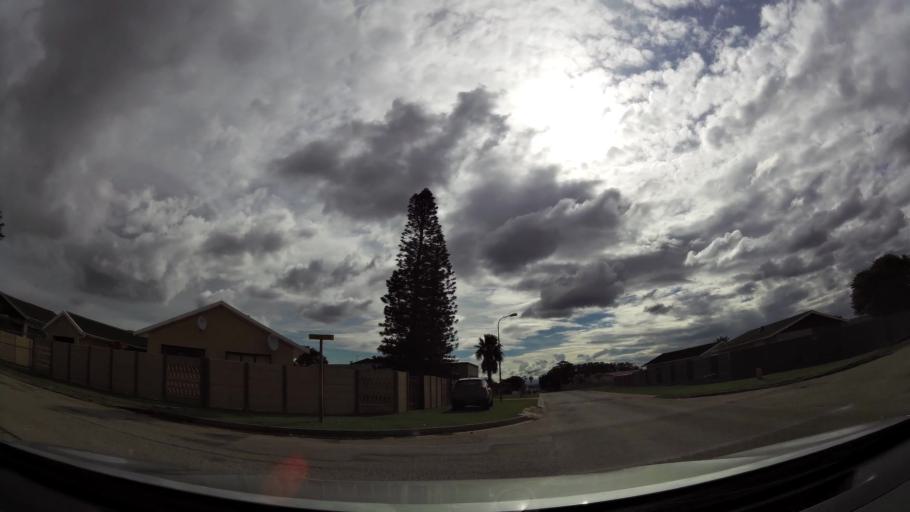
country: ZA
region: Eastern Cape
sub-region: Nelson Mandela Bay Metropolitan Municipality
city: Port Elizabeth
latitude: -33.9352
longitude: 25.5076
